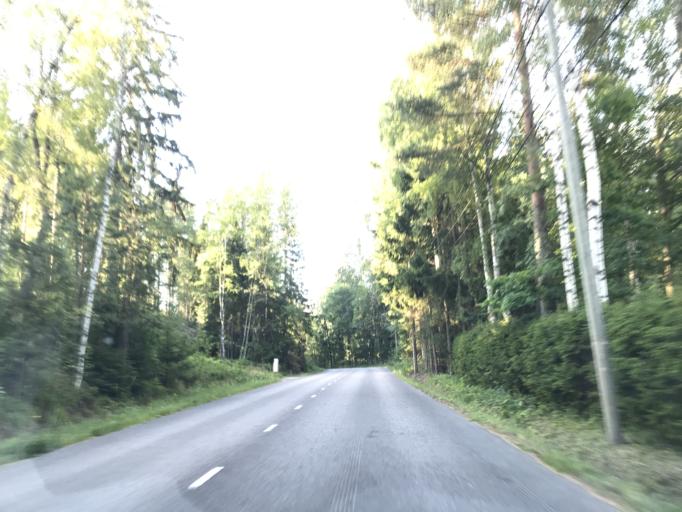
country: FI
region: Uusimaa
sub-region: Helsinki
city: Kauniainen
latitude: 60.3417
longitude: 24.7043
